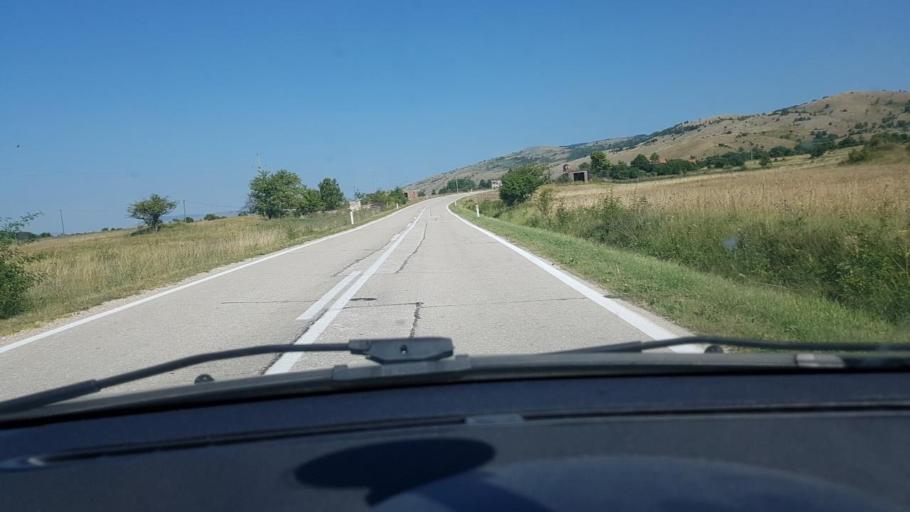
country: BA
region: Federation of Bosnia and Herzegovina
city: Bosansko Grahovo
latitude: 44.1147
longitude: 16.5389
